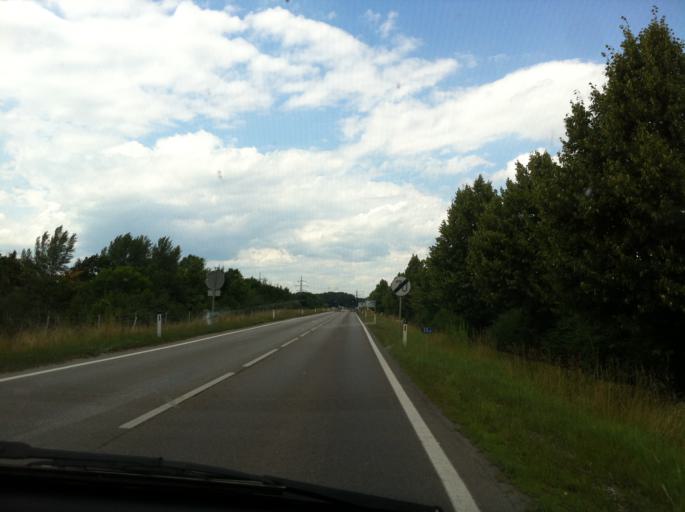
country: AT
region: Lower Austria
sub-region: Politischer Bezirk Tulln
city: Langenrohr
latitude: 48.3182
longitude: 16.0302
